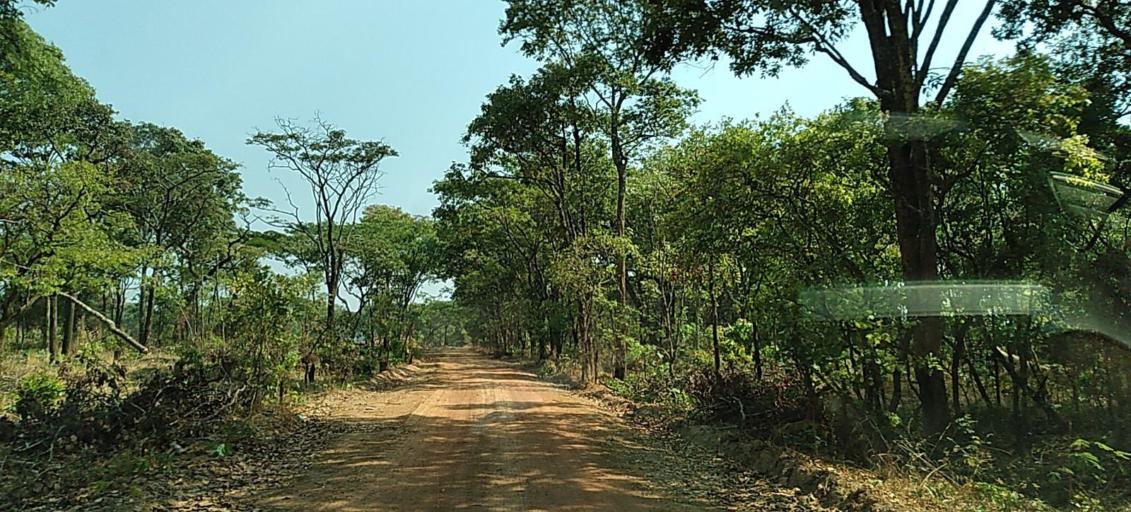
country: ZM
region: Copperbelt
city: Kalulushi
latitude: -12.9253
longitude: 27.8220
